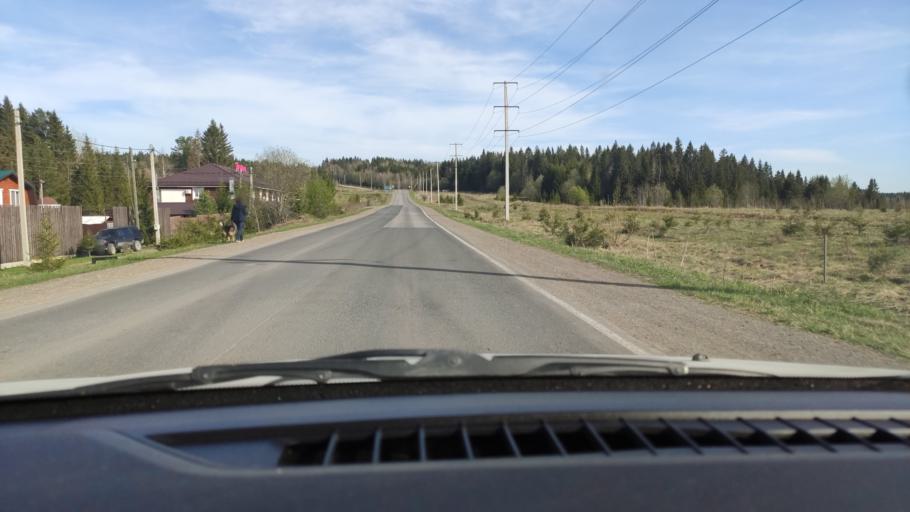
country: RU
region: Perm
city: Novyye Lyady
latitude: 57.9334
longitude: 56.6356
